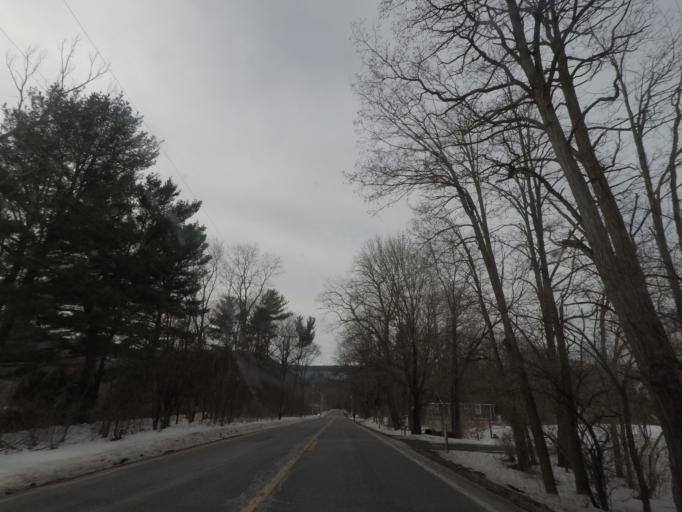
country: US
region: New York
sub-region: Albany County
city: Altamont
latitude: 42.6583
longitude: -73.9925
